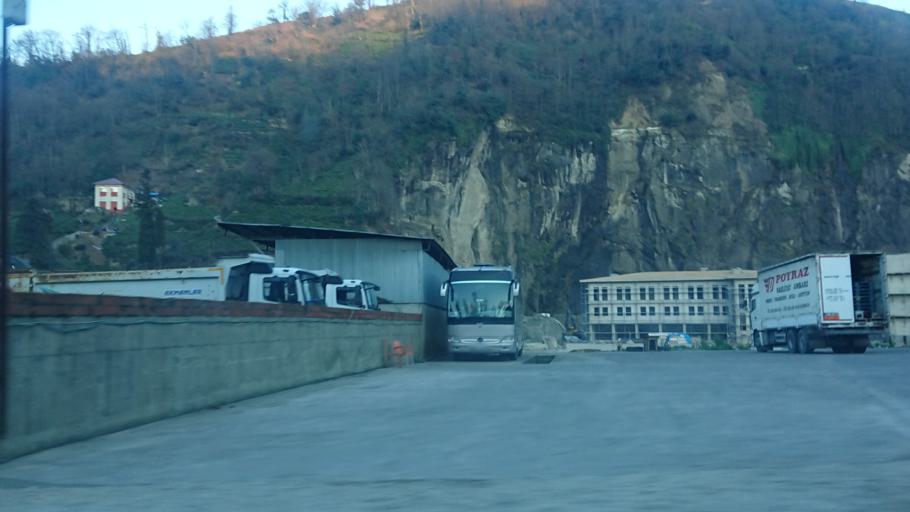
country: TR
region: Rize
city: Gundogdu
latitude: 41.0299
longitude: 40.5821
